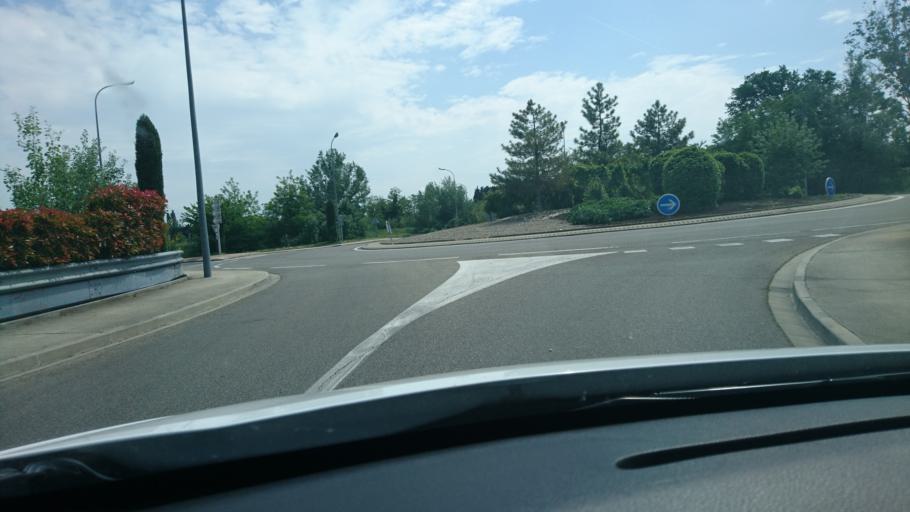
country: FR
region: Provence-Alpes-Cote d'Azur
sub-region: Departement du Vaucluse
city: Morieres-les-Avignon
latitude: 43.9533
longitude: 4.8846
